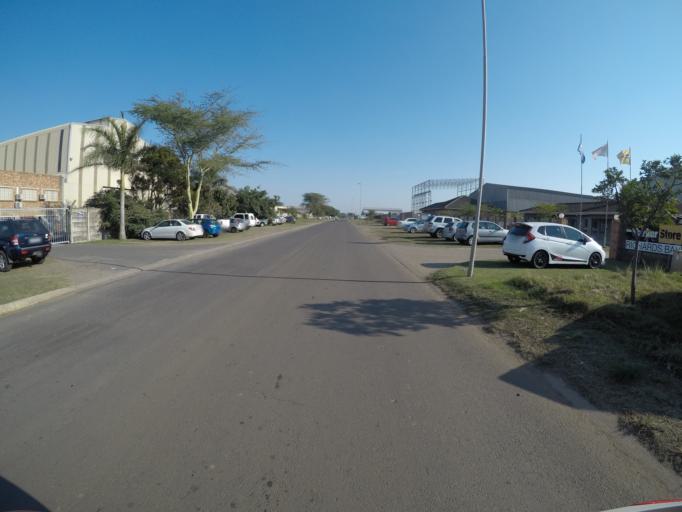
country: ZA
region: KwaZulu-Natal
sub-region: uThungulu District Municipality
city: Richards Bay
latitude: -28.7507
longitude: 32.0261
